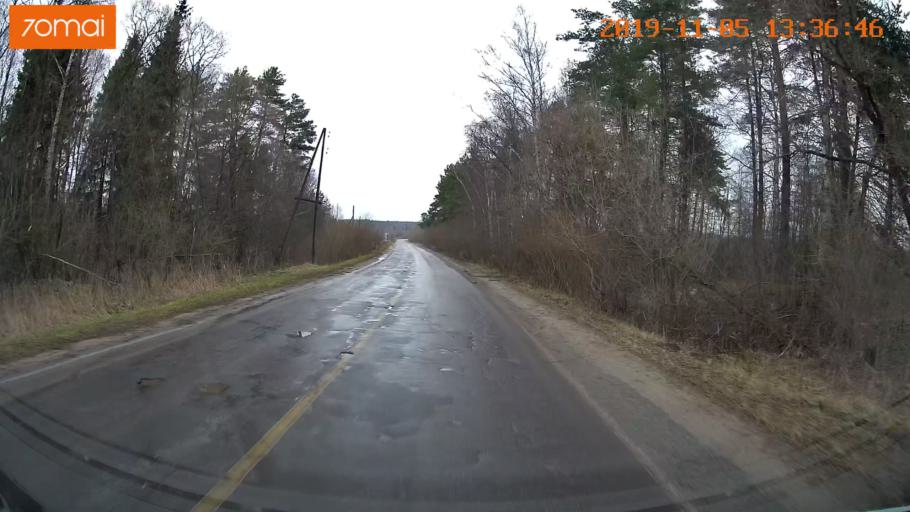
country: RU
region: Ivanovo
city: Shuya
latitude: 56.9171
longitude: 41.3822
